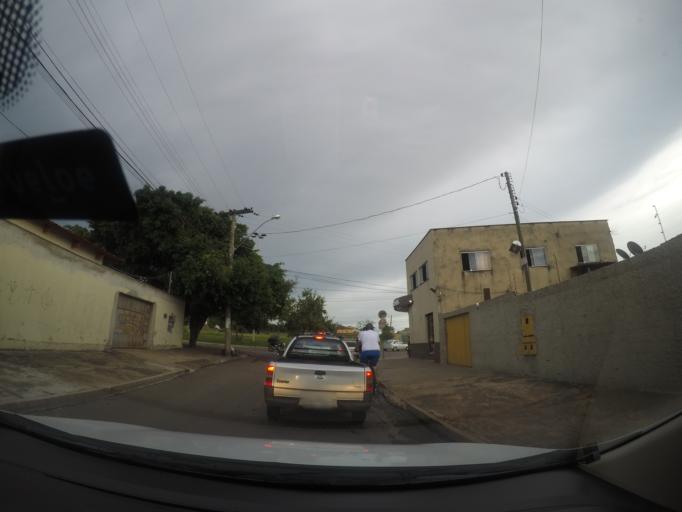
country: BR
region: Goias
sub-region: Goiania
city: Goiania
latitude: -16.7310
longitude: -49.3089
